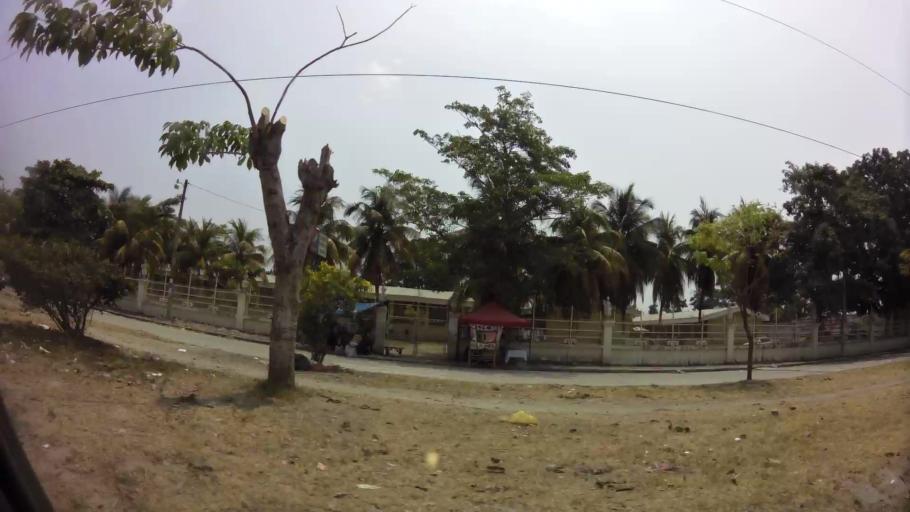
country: HN
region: Cortes
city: San Pedro Sula
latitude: 15.4884
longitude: -87.9856
